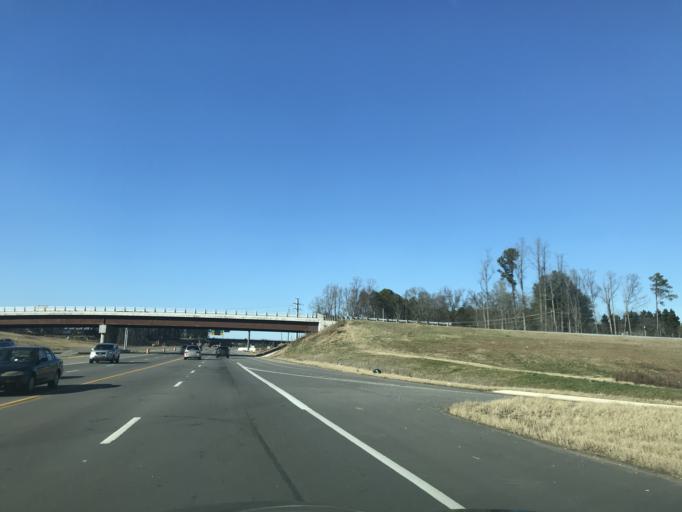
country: US
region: North Carolina
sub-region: Durham County
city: Durham
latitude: 35.9803
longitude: -78.8561
